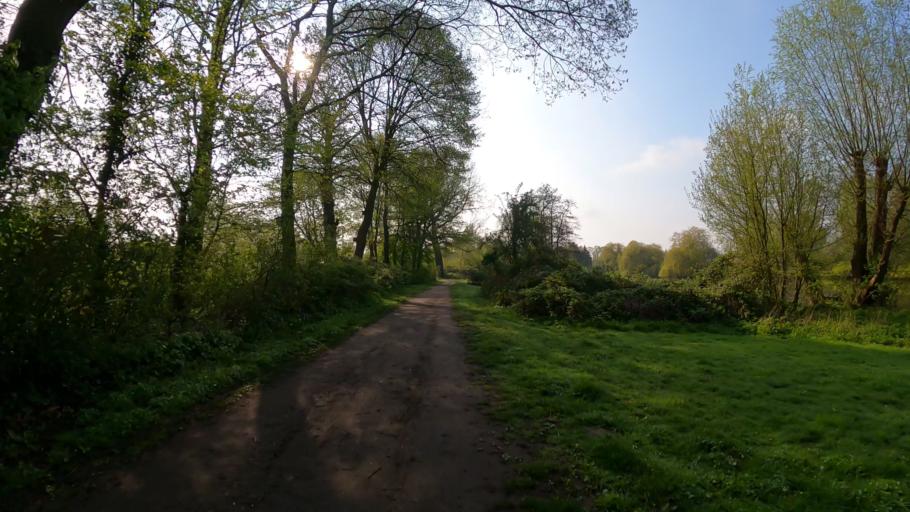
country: DE
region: Hamburg
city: Kleiner Grasbrook
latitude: 53.5084
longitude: 10.0129
